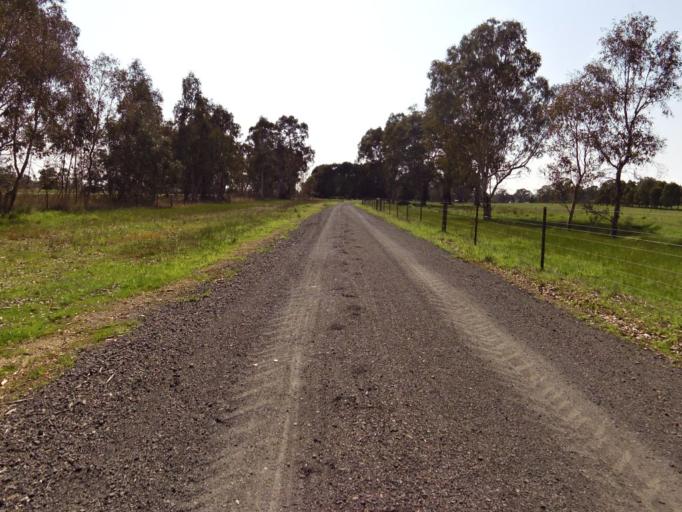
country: AU
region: Victoria
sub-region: Murrindindi
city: Alexandra
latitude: -37.1128
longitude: 145.6086
